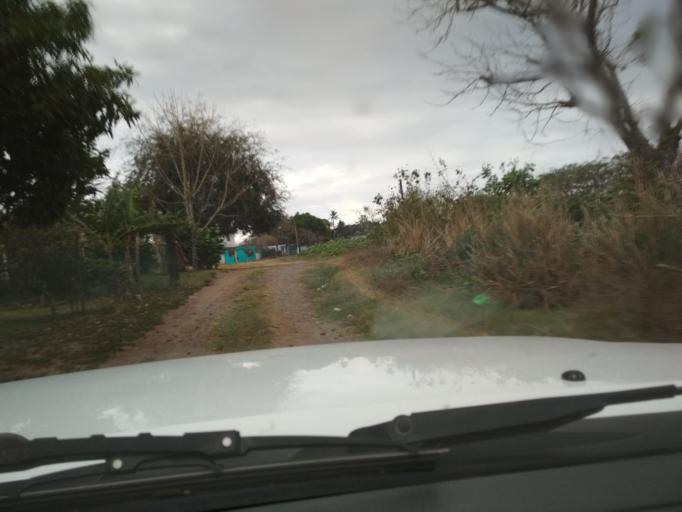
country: MX
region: Veracruz
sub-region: Veracruz
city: Delfino Victoria (Santa Fe)
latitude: 19.1644
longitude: -96.2609
